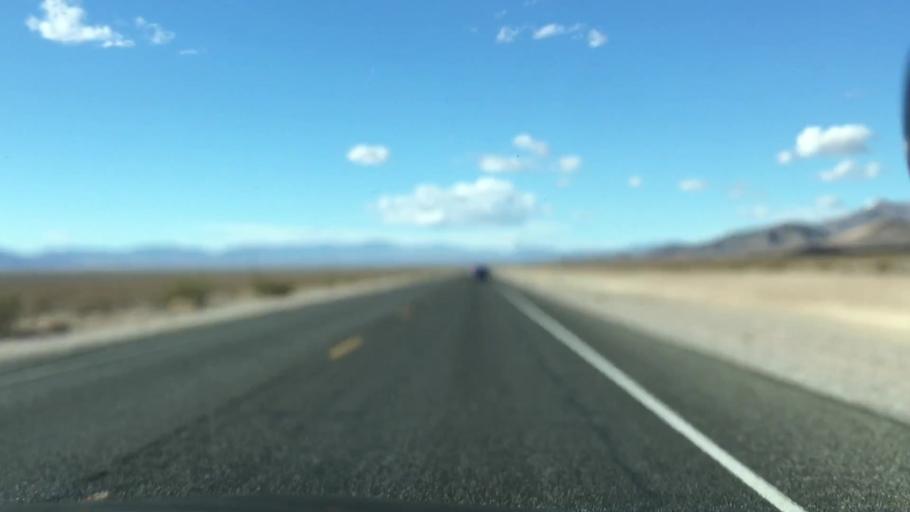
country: US
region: Nevada
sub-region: Nye County
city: Beatty
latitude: 36.6975
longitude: -116.5767
